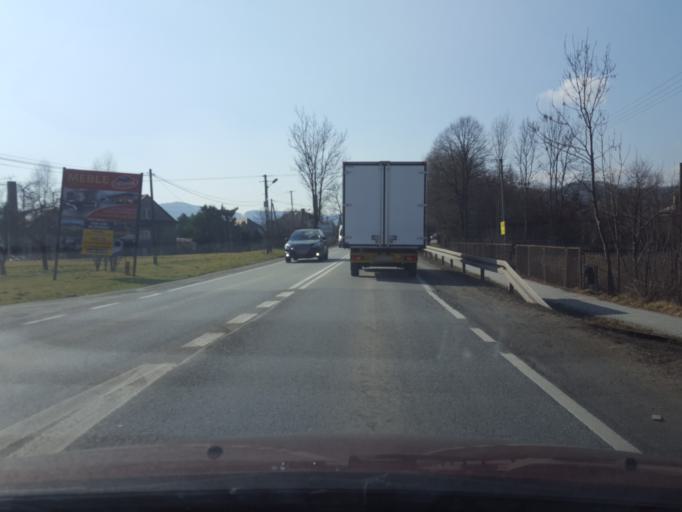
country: PL
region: Lesser Poland Voivodeship
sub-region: Powiat brzeski
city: Czchow
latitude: 49.8418
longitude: 20.6811
